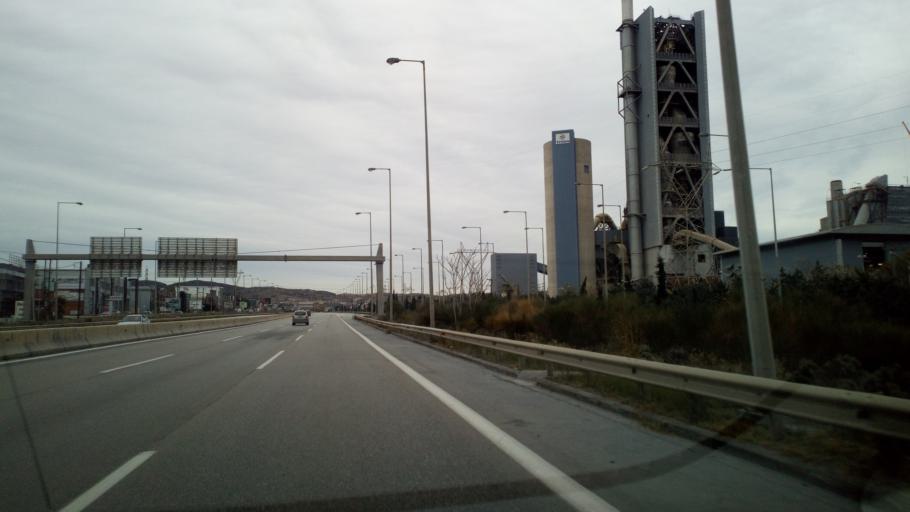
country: GR
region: Central Macedonia
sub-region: Nomos Thessalonikis
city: Efkarpia
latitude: 40.6981
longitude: 22.9492
